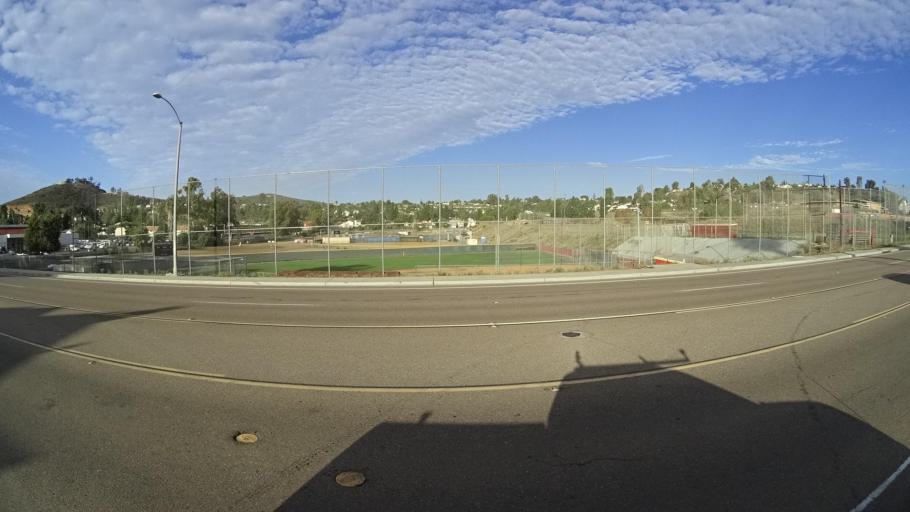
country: US
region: California
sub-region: San Diego County
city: Spring Valley
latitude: 32.7330
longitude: -116.9715
